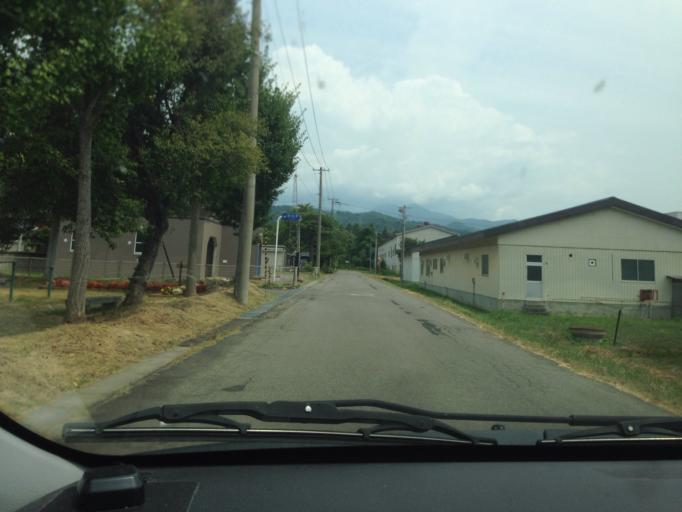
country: JP
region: Fukushima
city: Kitakata
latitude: 37.7172
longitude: 139.8754
